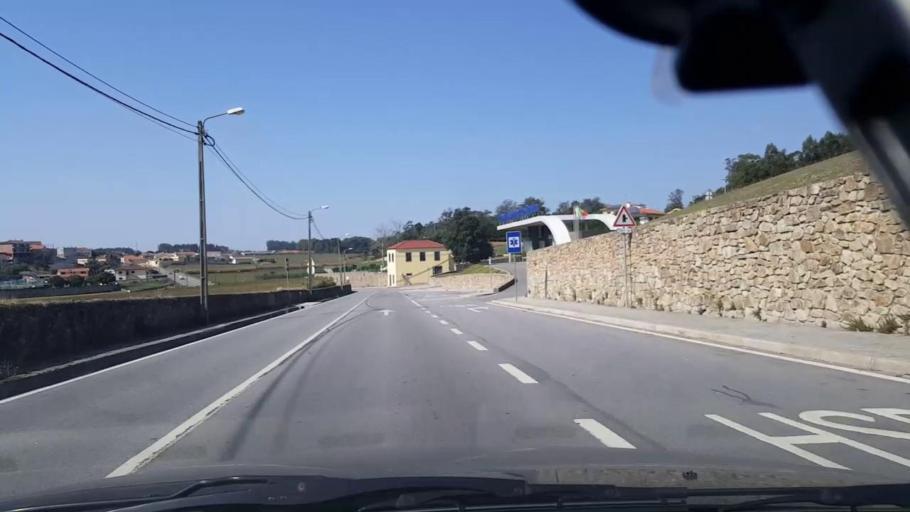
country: PT
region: Porto
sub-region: Vila do Conde
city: Vila do Conde
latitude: 41.3863
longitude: -8.7121
